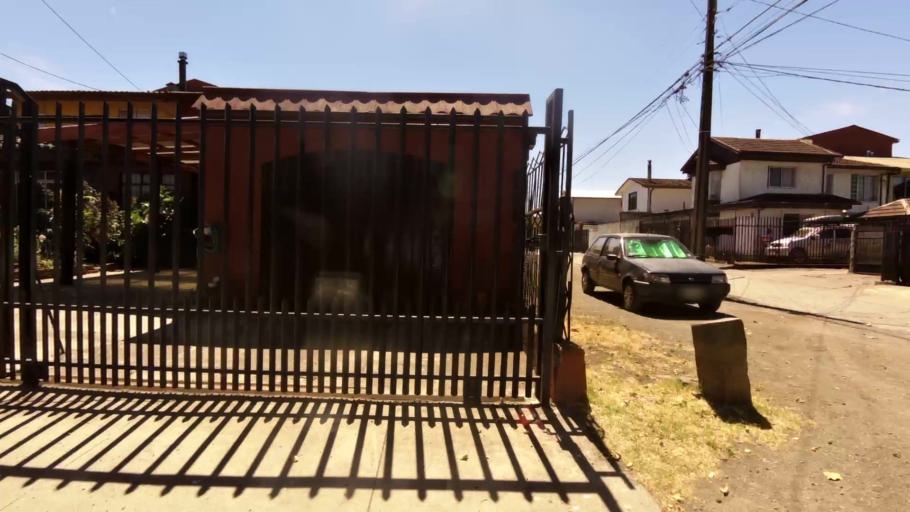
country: CL
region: Biobio
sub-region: Provincia de Concepcion
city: Talcahuano
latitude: -36.7596
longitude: -73.0933
